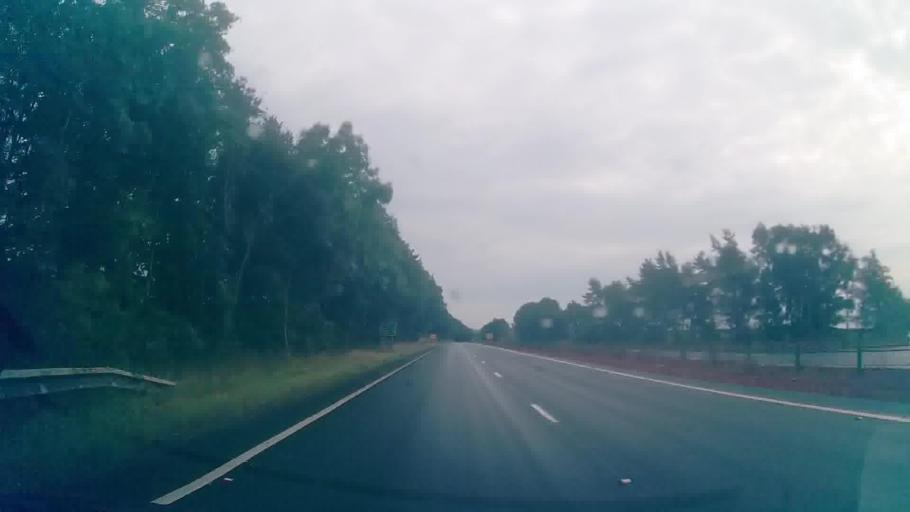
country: GB
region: Scotland
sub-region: Dumfries and Galloway
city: Locharbriggs
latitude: 55.0665
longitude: -3.5179
